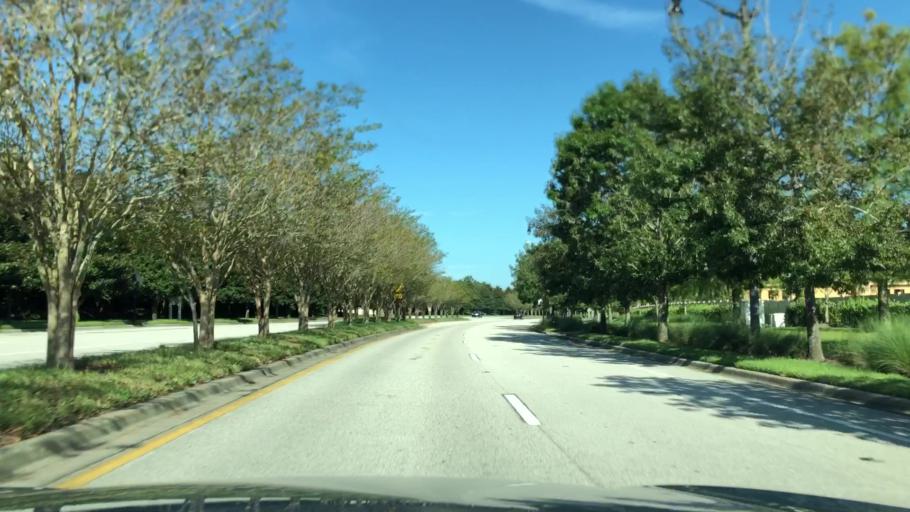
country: US
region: Florida
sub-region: Saint Johns County
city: Palm Valley
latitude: 30.1049
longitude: -81.4277
